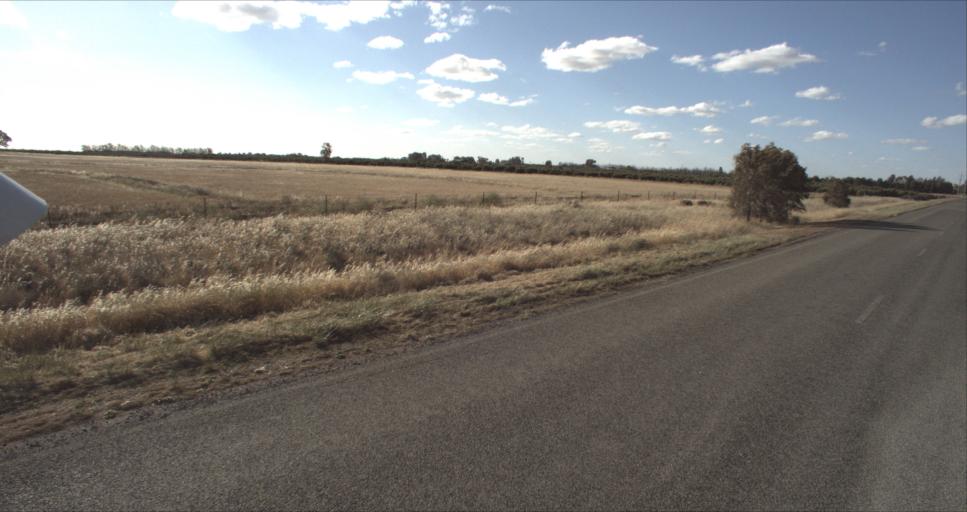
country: AU
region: New South Wales
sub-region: Leeton
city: Leeton
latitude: -34.5313
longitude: 146.2814
